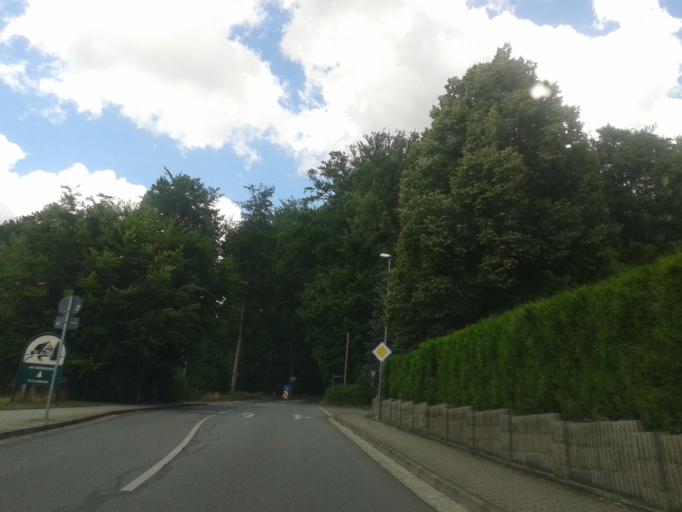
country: DE
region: Saxony
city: Radeberg
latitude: 51.0825
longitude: 13.9018
